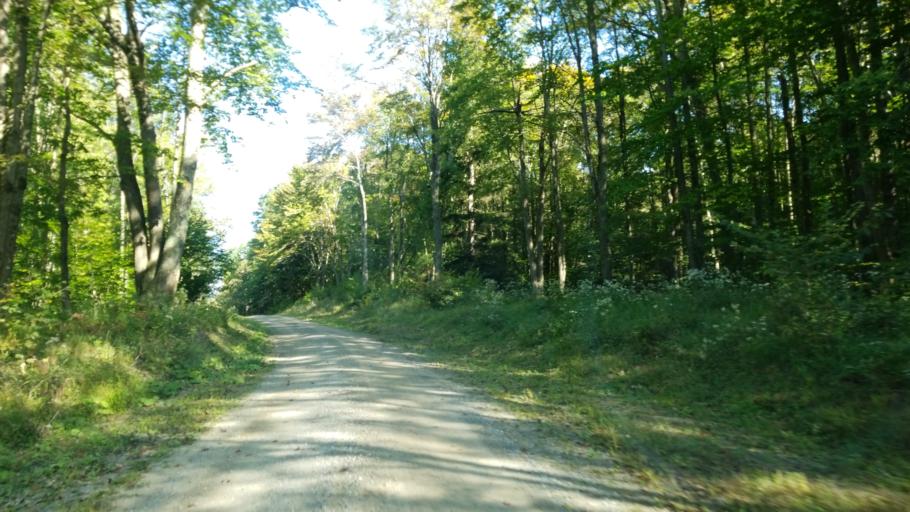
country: US
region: Pennsylvania
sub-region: Clearfield County
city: Curwensville
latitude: 41.1271
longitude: -78.5647
